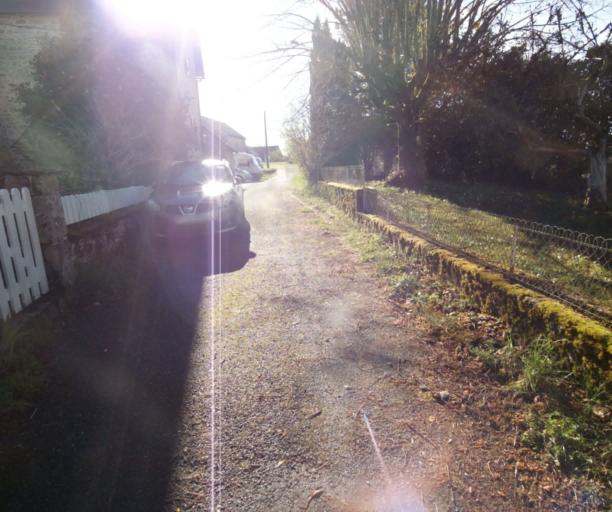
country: FR
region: Limousin
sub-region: Departement de la Correze
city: Correze
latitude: 45.2700
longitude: 1.8837
